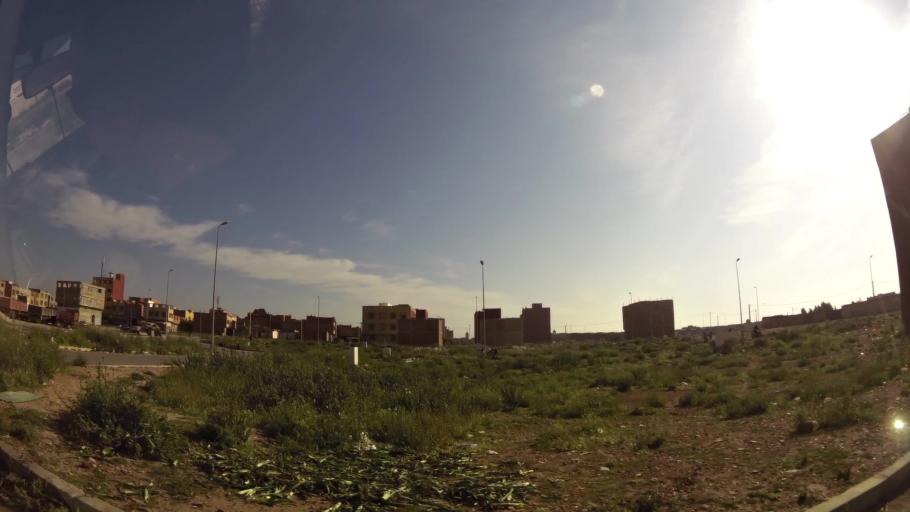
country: MA
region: Oriental
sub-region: Oujda-Angad
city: Oujda
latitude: 34.7175
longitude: -1.8932
